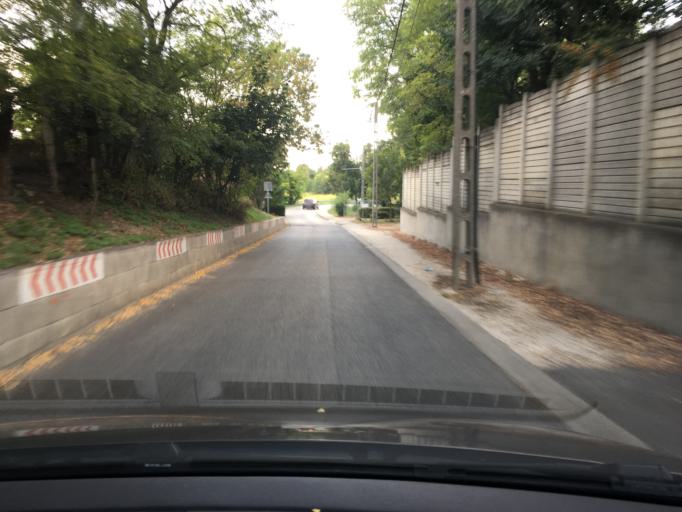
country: HU
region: Pest
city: Szada
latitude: 47.6398
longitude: 19.3098
